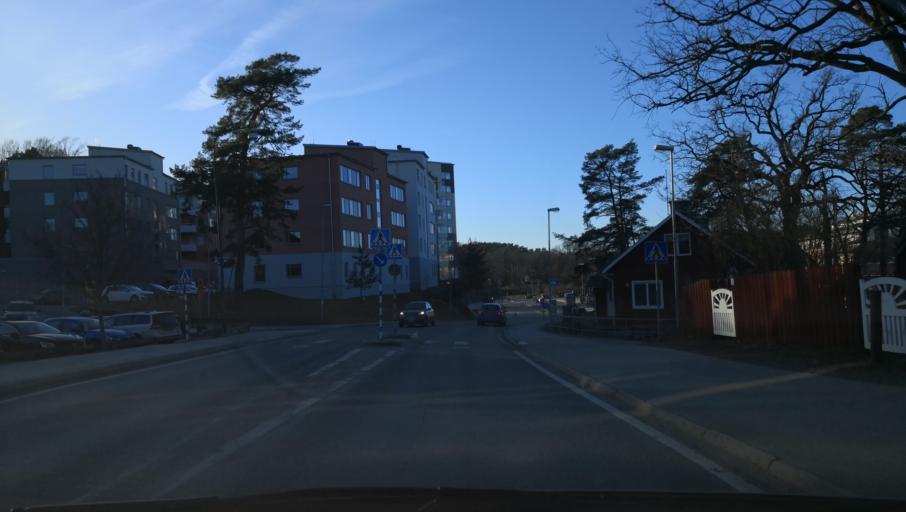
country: SE
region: Stockholm
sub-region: Varmdo Kommun
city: Gustavsberg
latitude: 59.3250
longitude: 18.3937
